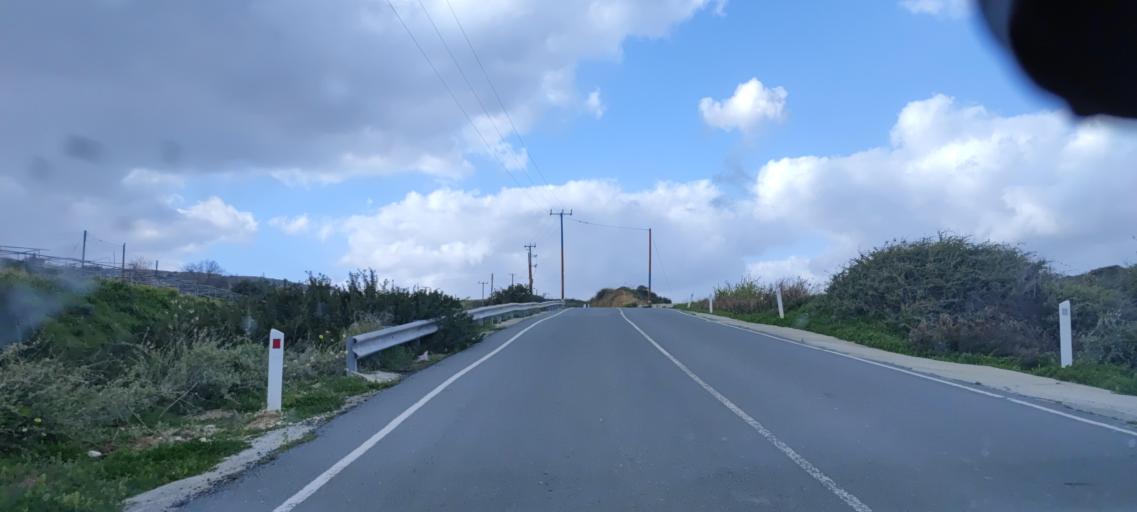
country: CY
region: Limassol
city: Pissouri
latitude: 34.6658
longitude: 32.7114
